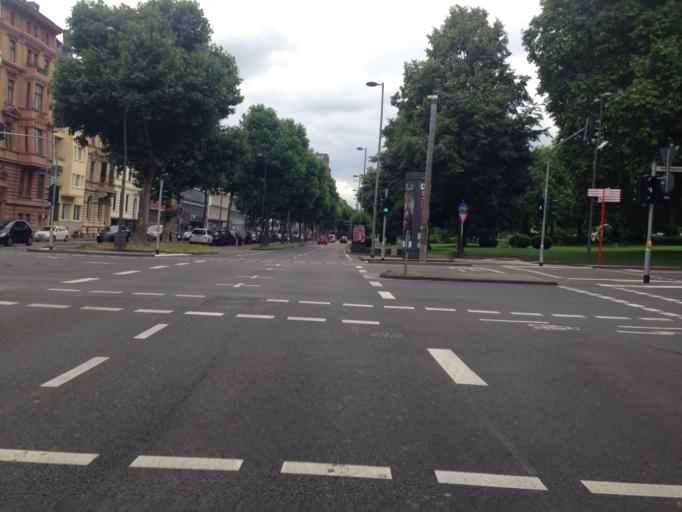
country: DE
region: North Rhine-Westphalia
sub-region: Regierungsbezirk Koln
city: Neustadt/Nord
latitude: 50.9463
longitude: 6.9458
